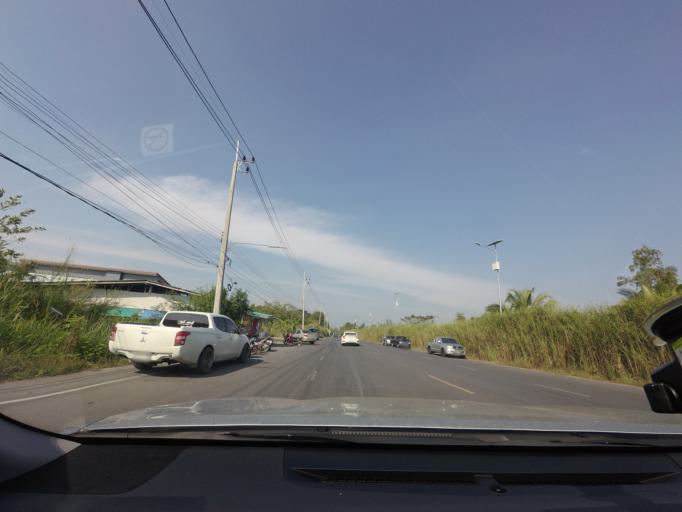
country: TH
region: Nakhon Si Thammarat
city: Nakhon Si Thammarat
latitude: 8.5120
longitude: 99.9681
